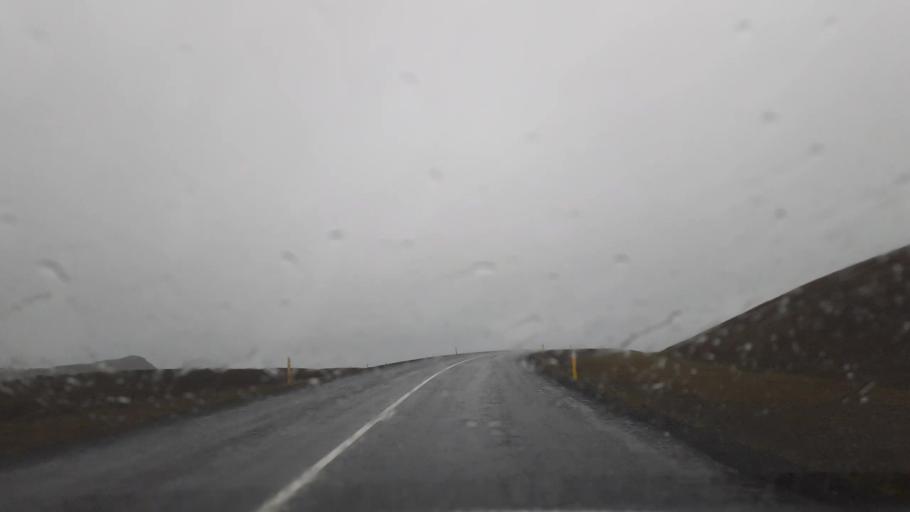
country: IS
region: Northeast
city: Husavik
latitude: 66.2335
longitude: -15.7884
